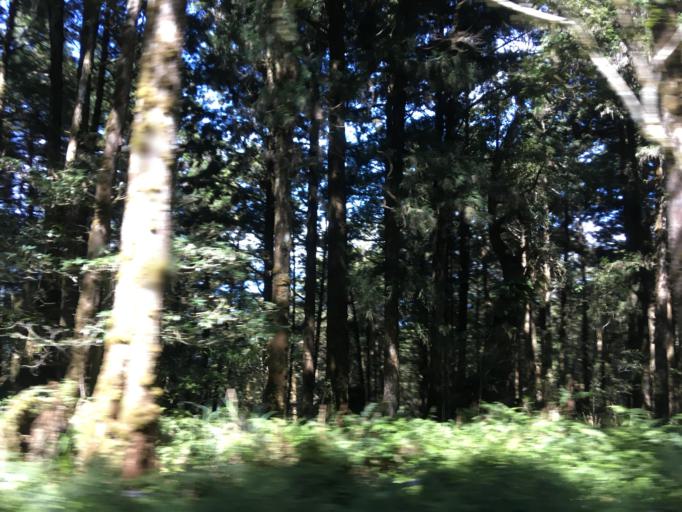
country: TW
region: Taiwan
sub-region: Yilan
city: Yilan
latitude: 24.5150
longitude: 121.5218
